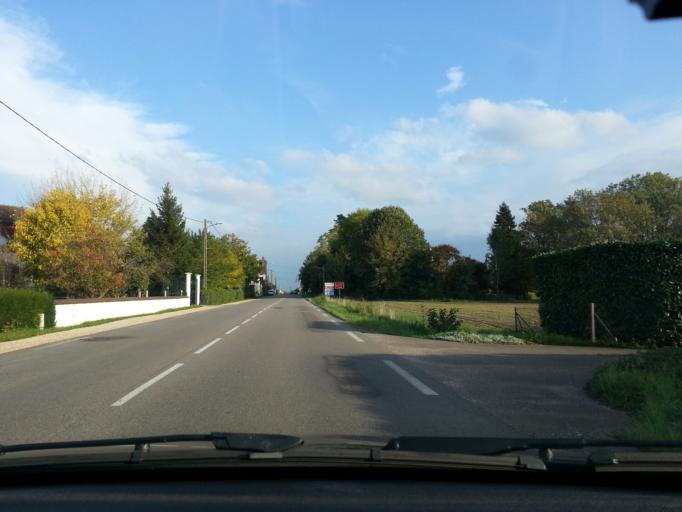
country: FR
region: Bourgogne
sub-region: Departement de Saone-et-Loire
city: Chatenoy-le-Royal
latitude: 46.7757
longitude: 4.8115
